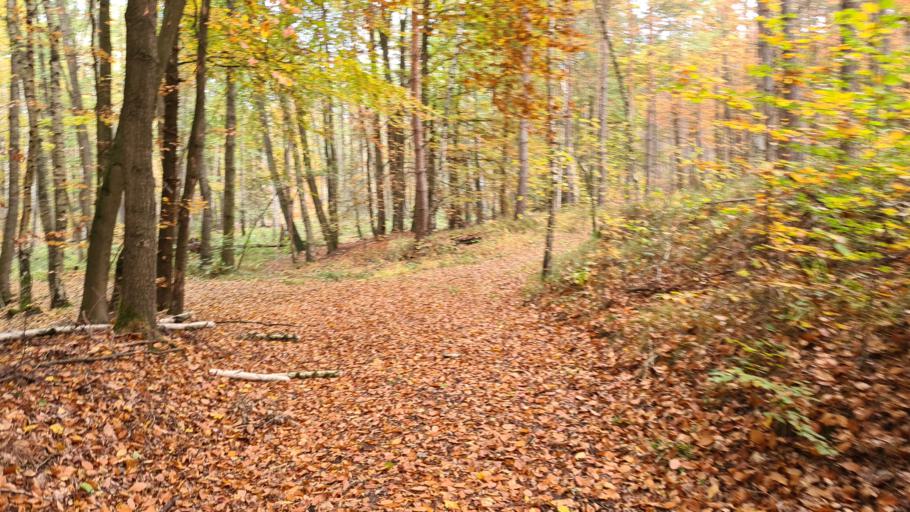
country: DE
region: Saxony
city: Dahlen
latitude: 51.4079
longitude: 12.9910
